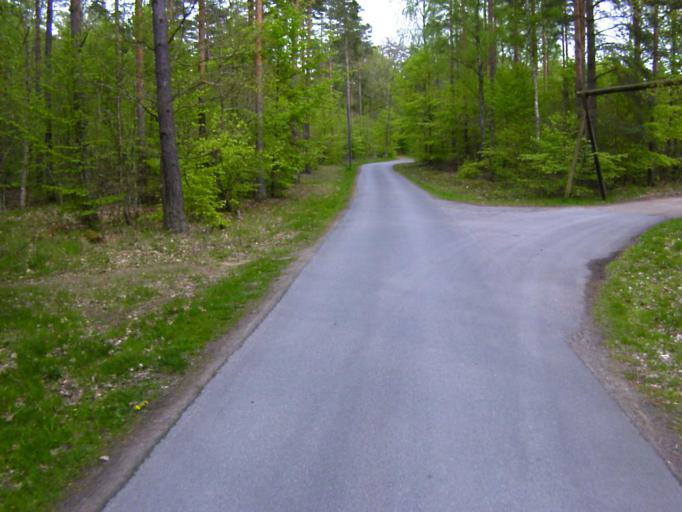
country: SE
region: Skane
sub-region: Kristianstads Kommun
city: Onnestad
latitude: 55.9198
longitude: 13.9717
